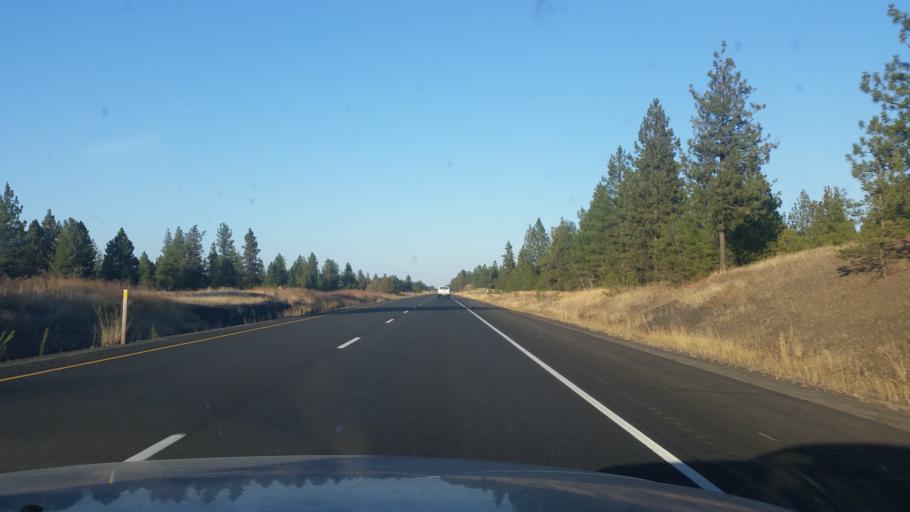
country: US
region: Washington
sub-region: Spokane County
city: Medical Lake
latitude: 47.4536
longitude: -117.7651
